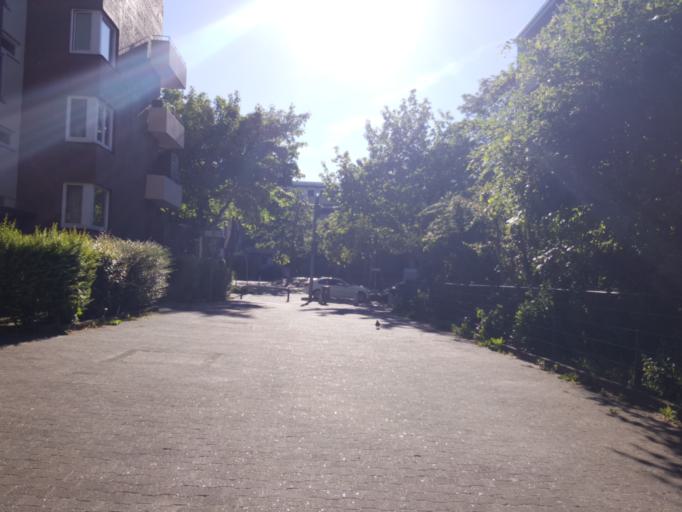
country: DE
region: Schleswig-Holstein
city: Oststeinbek
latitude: 53.5262
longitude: 10.1469
